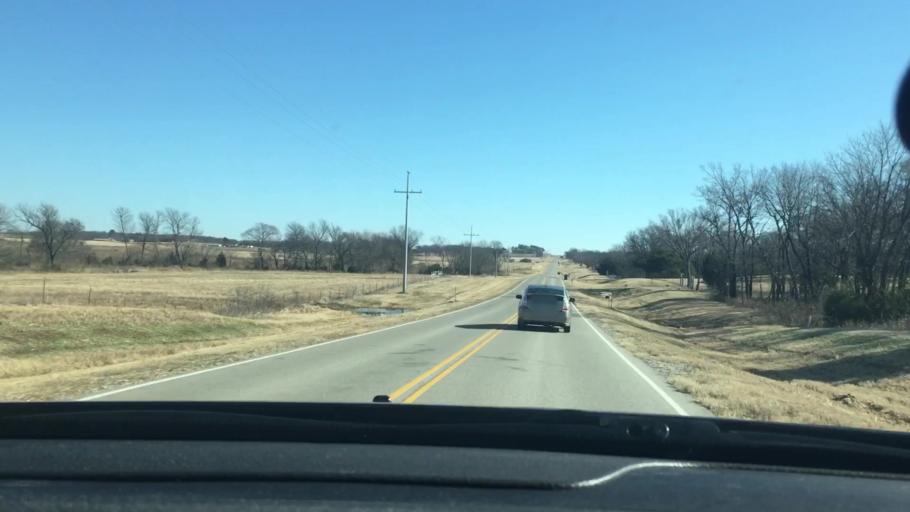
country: US
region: Oklahoma
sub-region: Murray County
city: Davis
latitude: 34.4772
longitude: -97.0733
